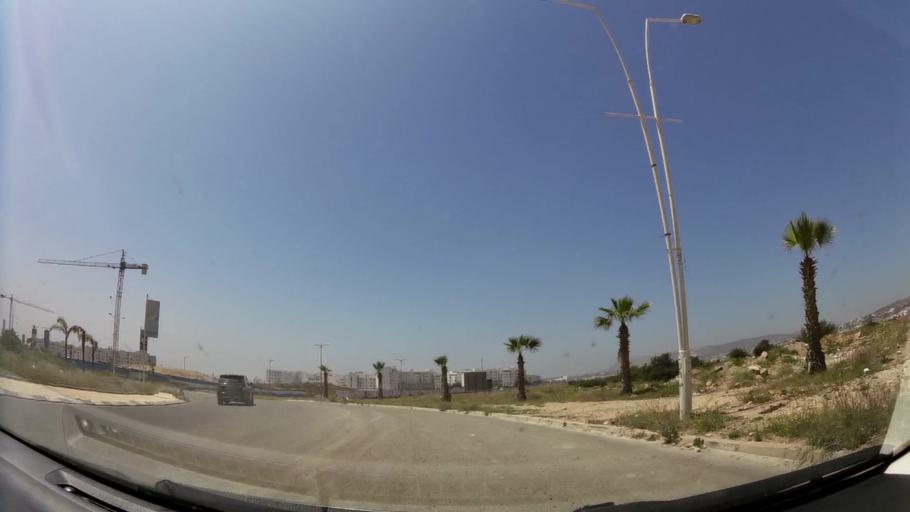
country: MA
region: Oued ed Dahab-Lagouira
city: Dakhla
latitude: 30.4386
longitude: -9.5662
